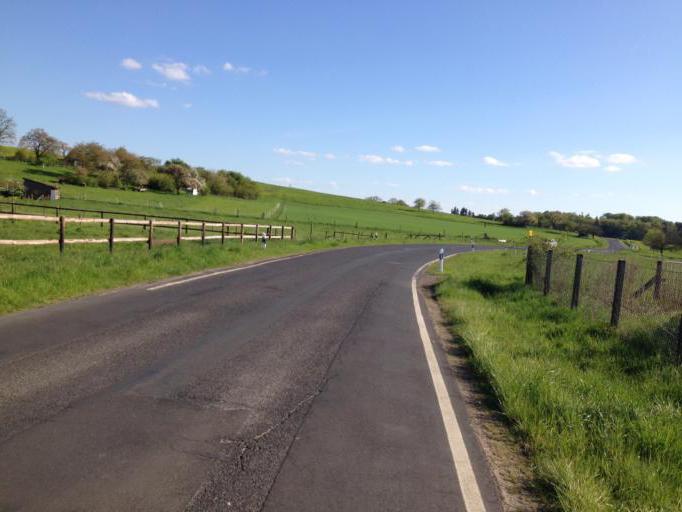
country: DE
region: Hesse
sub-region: Regierungsbezirk Giessen
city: Reiskirchen
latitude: 50.5726
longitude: 8.8483
